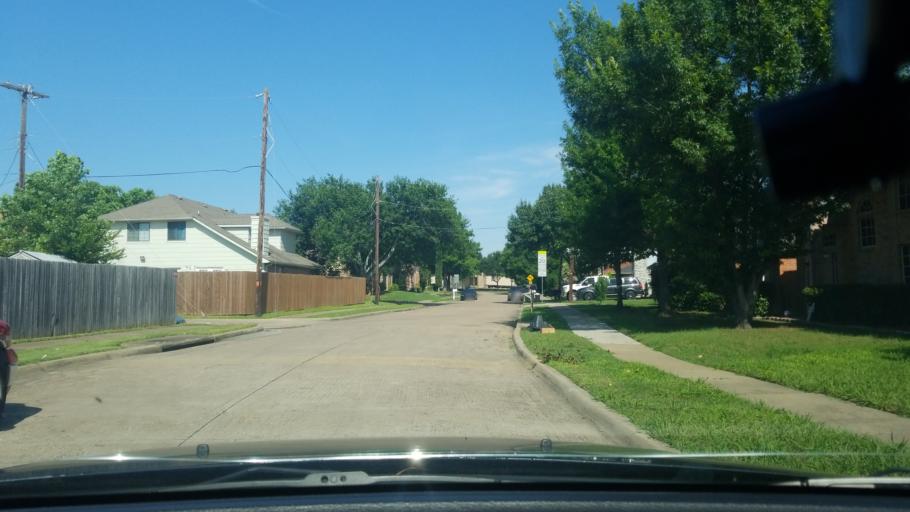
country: US
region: Texas
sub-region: Dallas County
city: Mesquite
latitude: 32.7737
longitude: -96.5779
